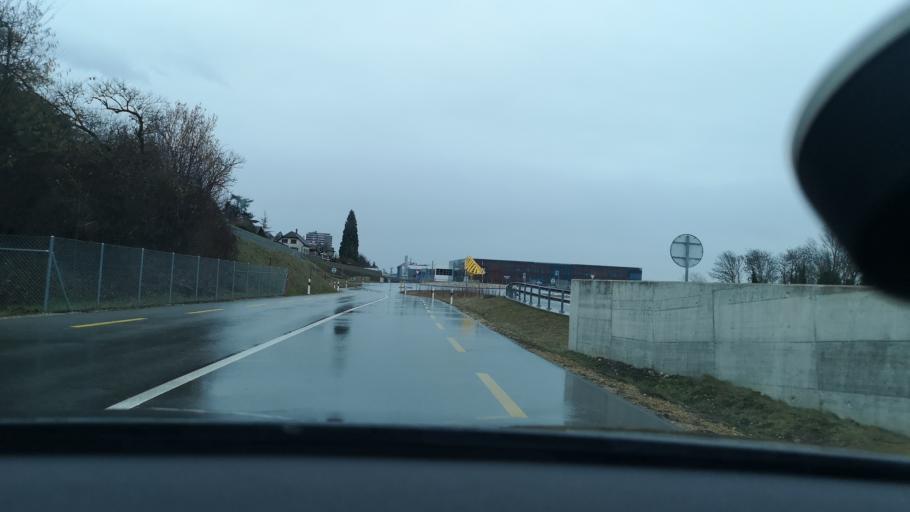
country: CH
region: Neuchatel
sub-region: Boudry District
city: Peseux
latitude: 46.9791
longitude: 6.8902
